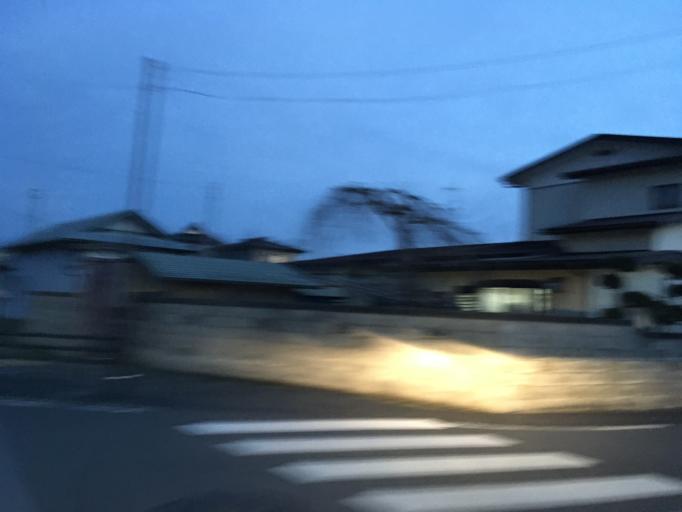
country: JP
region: Miyagi
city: Wakuya
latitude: 38.7204
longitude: 141.1407
